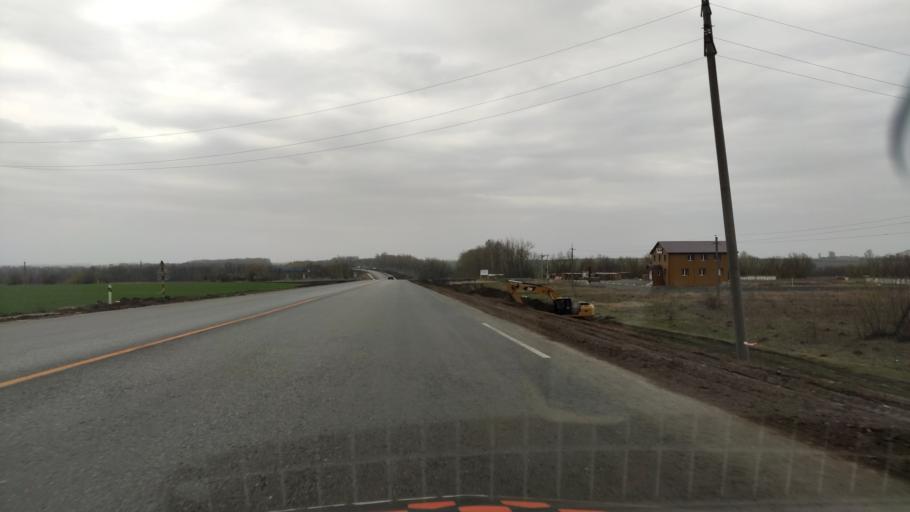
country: RU
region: Kursk
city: Gorshechnoye
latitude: 51.5511
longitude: 38.0409
